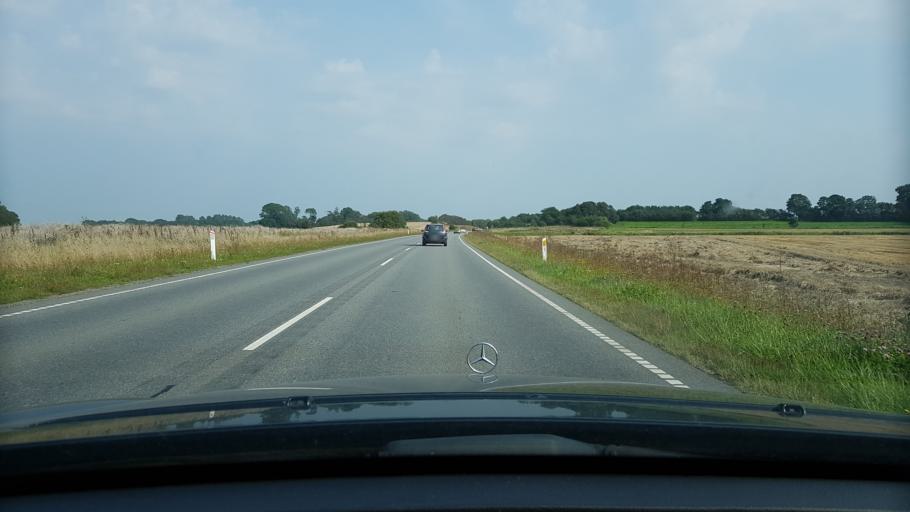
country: DK
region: North Denmark
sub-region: Alborg Kommune
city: Klarup
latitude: 57.0223
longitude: 10.0342
